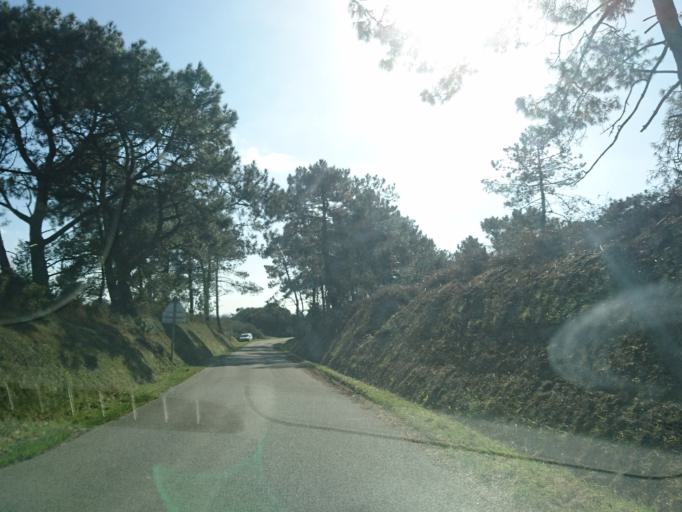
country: FR
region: Brittany
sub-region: Departement du Finistere
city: Roscanvel
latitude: 48.3397
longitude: -4.5353
